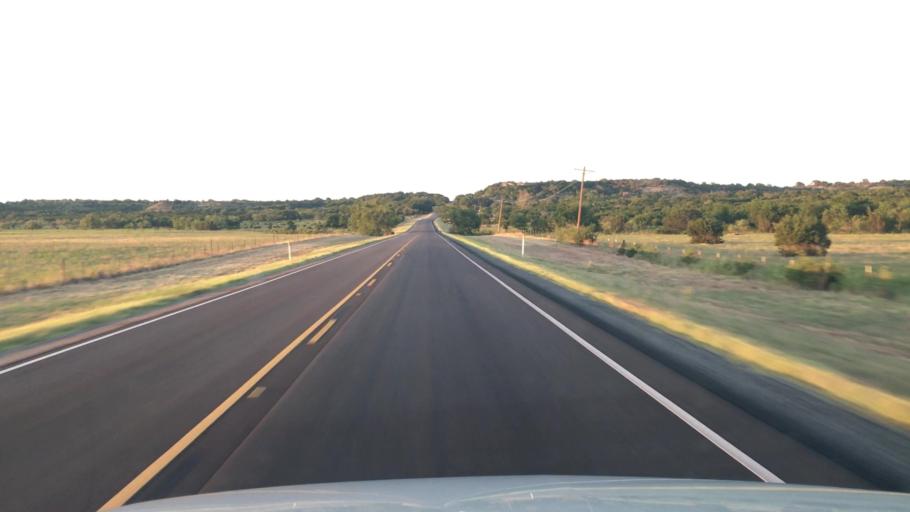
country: US
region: Texas
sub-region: Hamilton County
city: Hico
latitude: 32.0886
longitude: -97.9732
